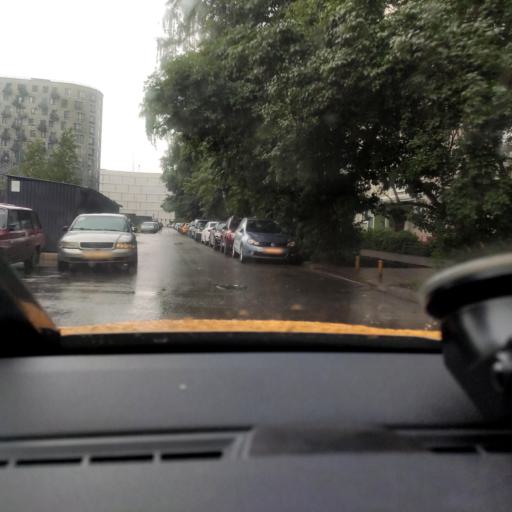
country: RU
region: Moskovskaya
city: Mytishchi
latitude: 55.9085
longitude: 37.7231
